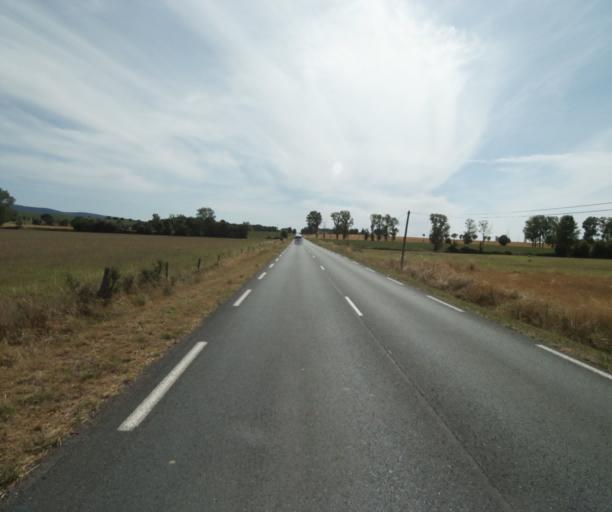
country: FR
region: Midi-Pyrenees
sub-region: Departement du Tarn
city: Soreze
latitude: 43.5064
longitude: 2.0566
